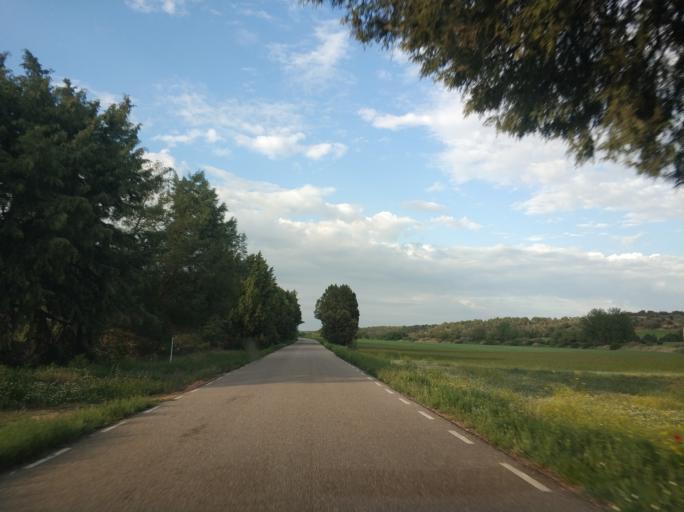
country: ES
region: Castille and Leon
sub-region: Provincia de Burgos
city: Brazacorta
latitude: 41.6925
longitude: -3.4061
